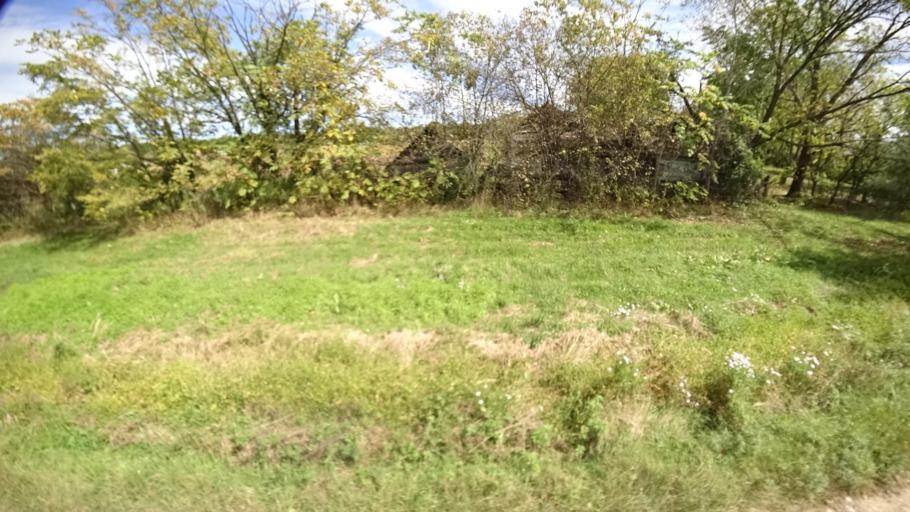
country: RU
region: Primorskiy
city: Yakovlevka
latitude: 44.6462
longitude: 133.5883
